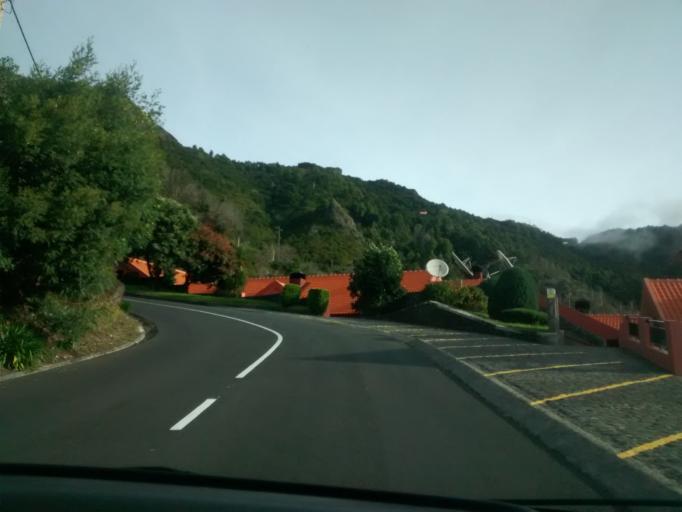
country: PT
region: Madeira
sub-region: Sao Vicente
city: Sao Vicente
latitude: 32.7493
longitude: -17.0251
